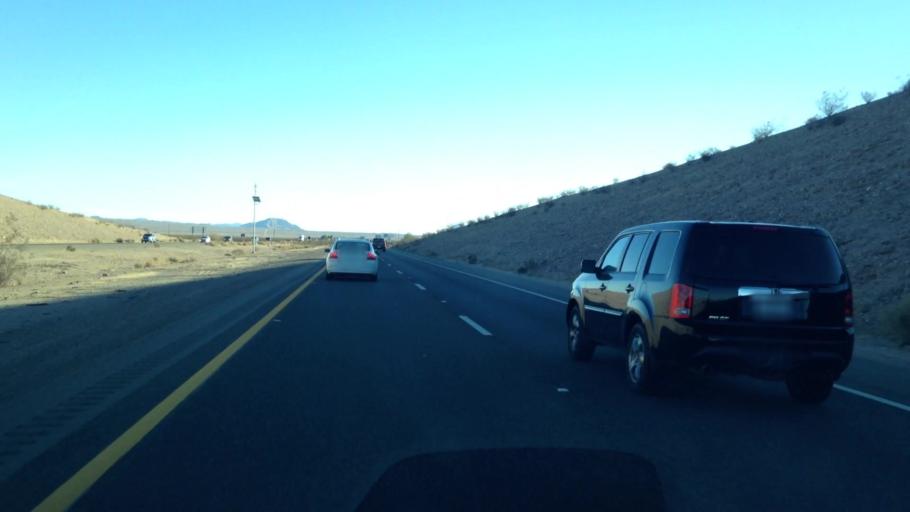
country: US
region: California
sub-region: San Bernardino County
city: Fort Irwin
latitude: 34.9717
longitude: -116.6260
